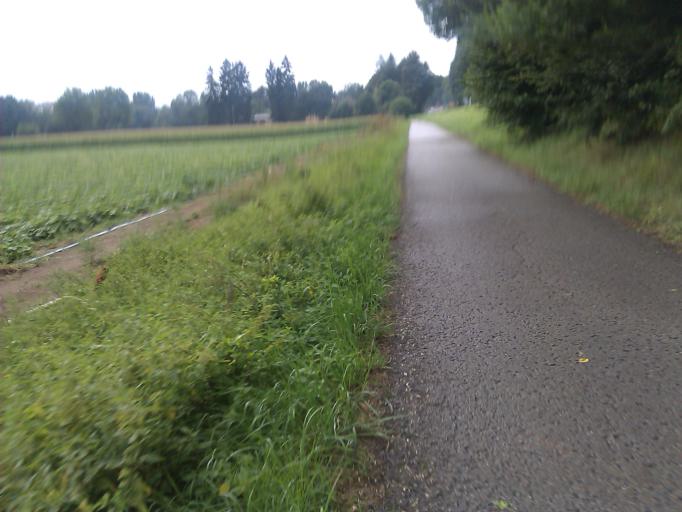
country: DE
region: Baden-Wuerttemberg
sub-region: Tuebingen Region
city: Pliezhausen
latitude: 48.5694
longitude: 9.2249
